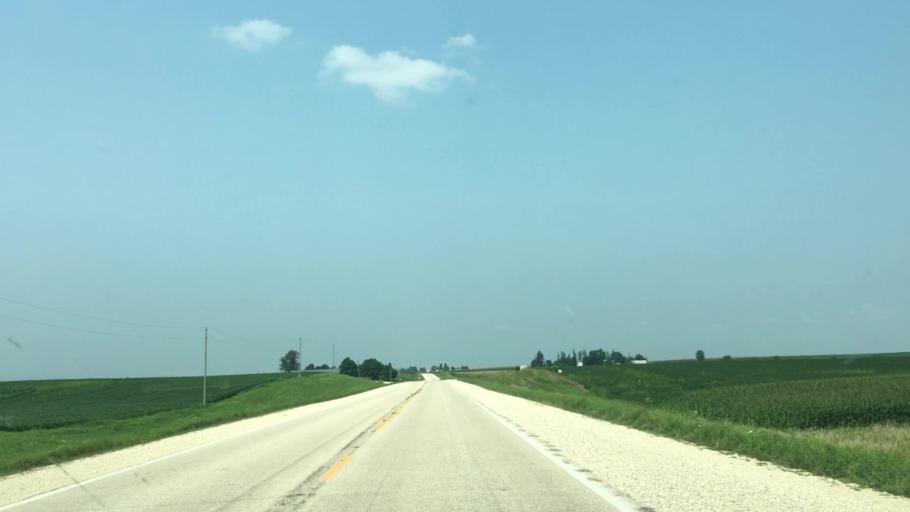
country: US
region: Iowa
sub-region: Fayette County
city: West Union
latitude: 42.9869
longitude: -91.8242
